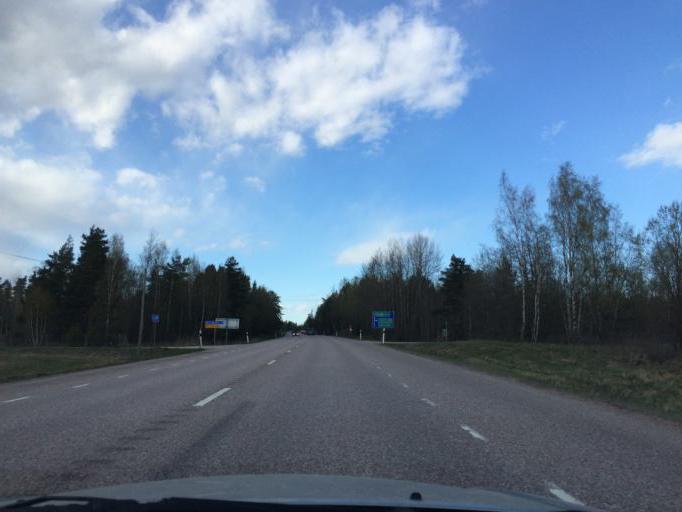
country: SE
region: Vaestmanland
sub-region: Hallstahammars Kommun
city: Kolback
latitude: 59.5747
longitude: 16.3524
